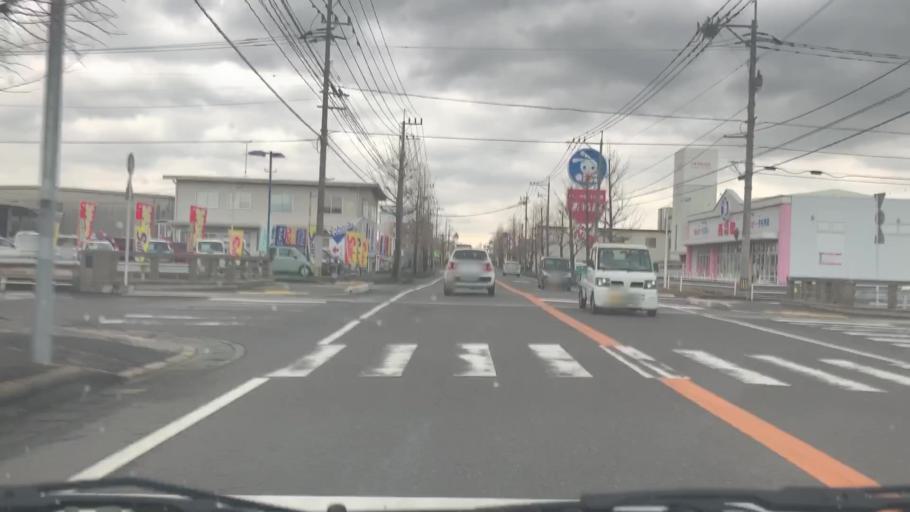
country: JP
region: Saga Prefecture
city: Saga-shi
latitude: 33.2558
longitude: 130.2658
